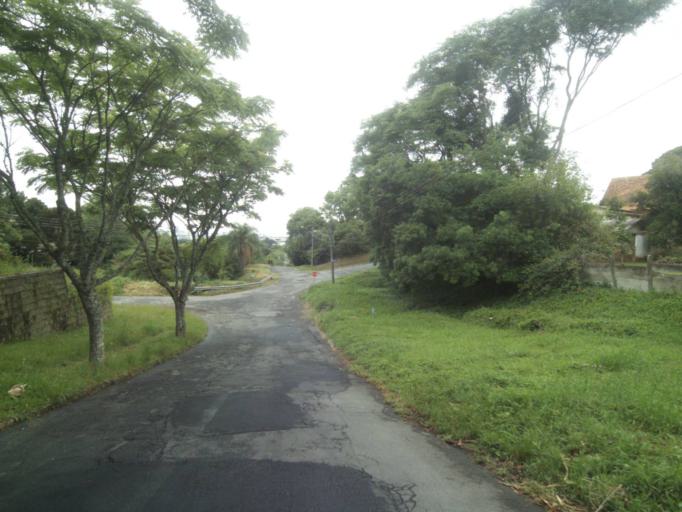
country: BR
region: Parana
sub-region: Curitiba
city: Curitiba
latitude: -25.4072
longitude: -49.2915
